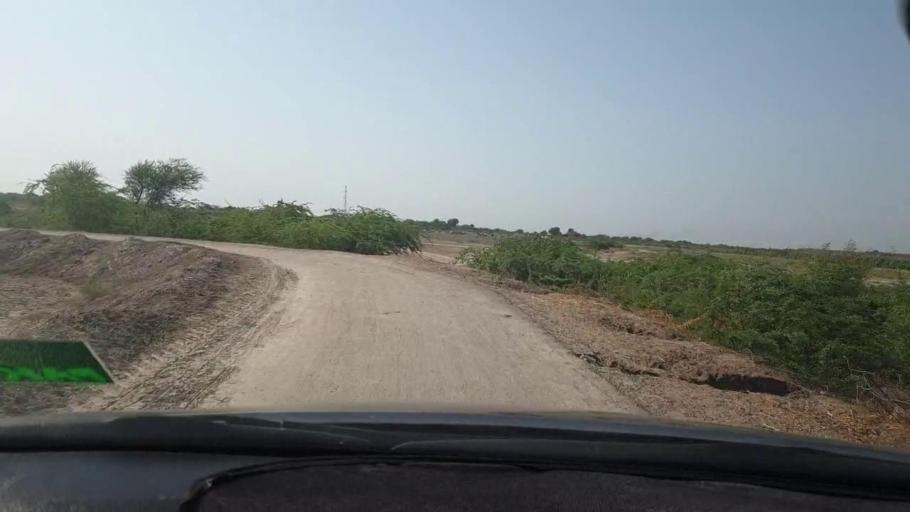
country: PK
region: Sindh
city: Naukot
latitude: 24.9447
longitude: 69.2466
